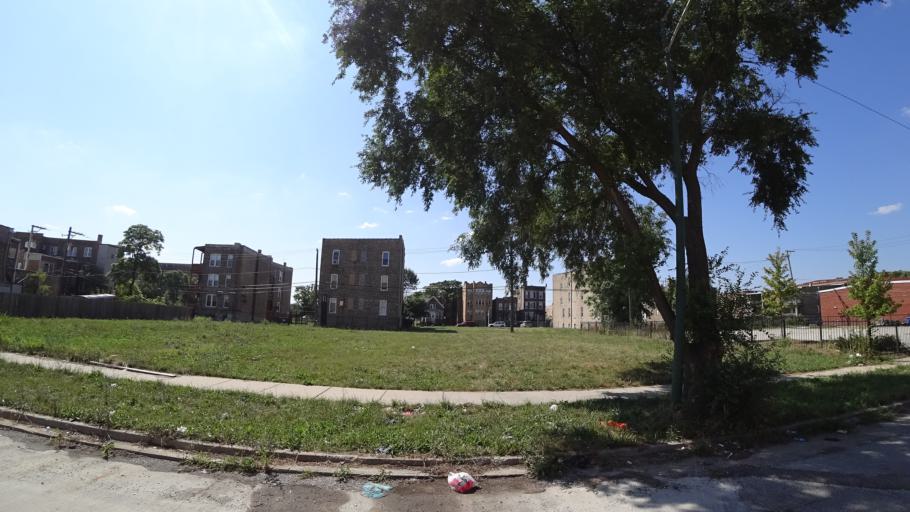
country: US
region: Illinois
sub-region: Cook County
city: Cicero
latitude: 41.8681
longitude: -87.7141
